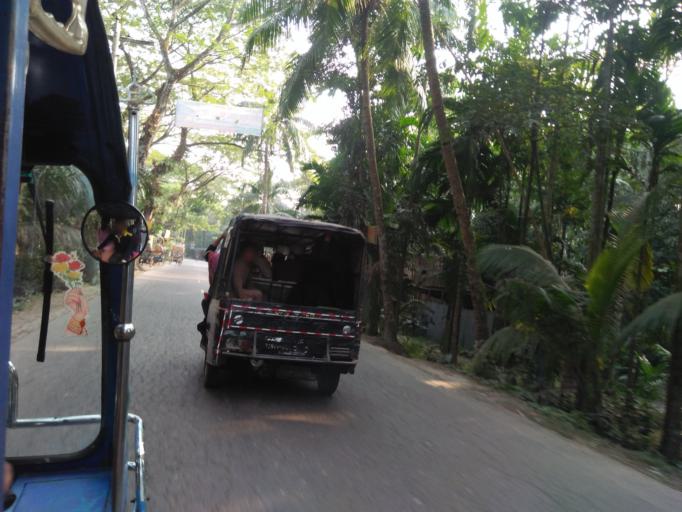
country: BD
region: Barisal
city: Bhola
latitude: 22.7018
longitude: 90.6414
